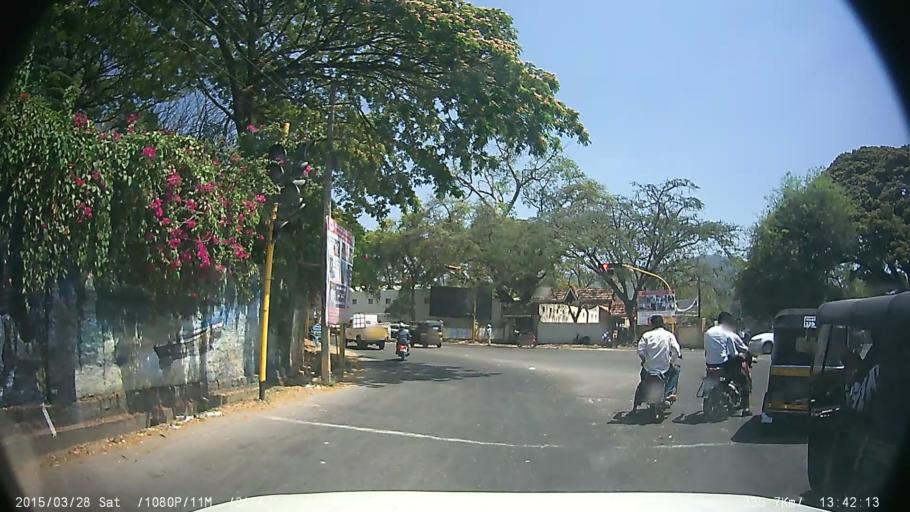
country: IN
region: Karnataka
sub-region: Mysore
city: Mysore
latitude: 12.2985
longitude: 76.6665
